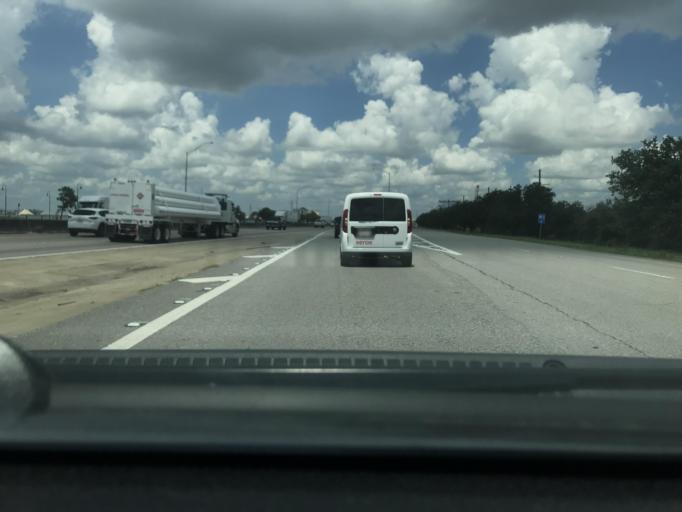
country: US
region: Louisiana
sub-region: Calcasieu Parish
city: Westlake
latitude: 30.2374
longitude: -93.2322
